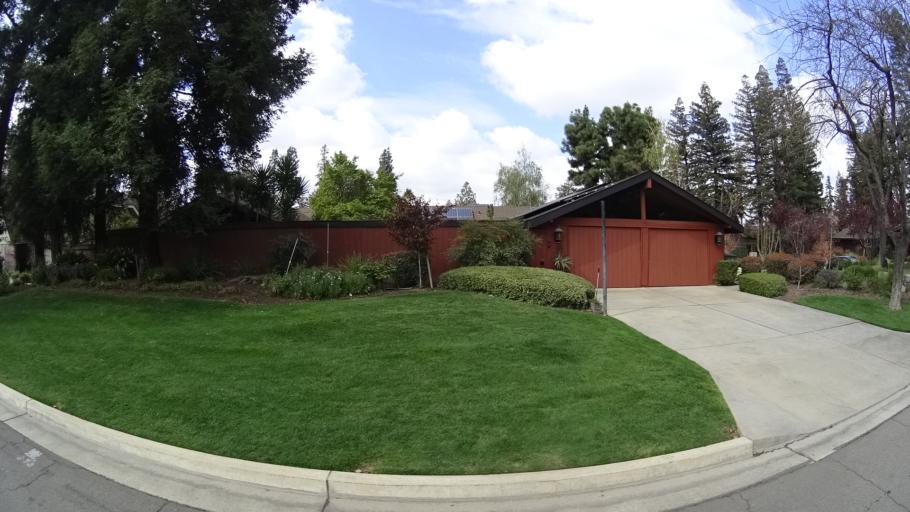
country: US
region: California
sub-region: Fresno County
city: Fresno
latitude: 36.8426
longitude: -119.8598
